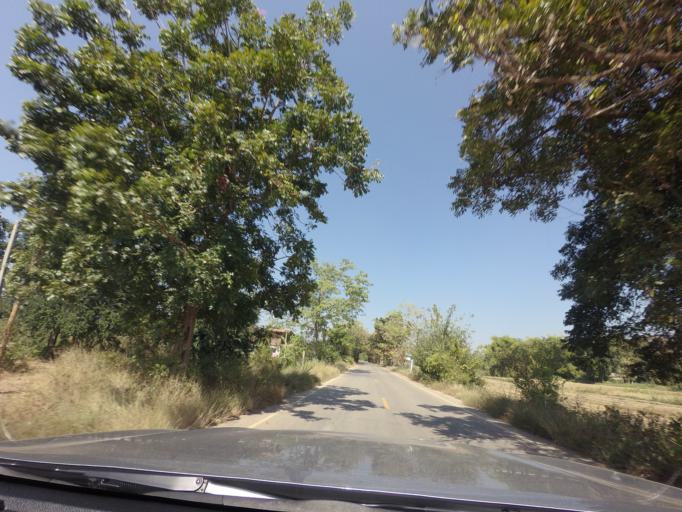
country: TH
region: Sukhothai
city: Si Samrong
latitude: 17.1412
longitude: 99.7706
